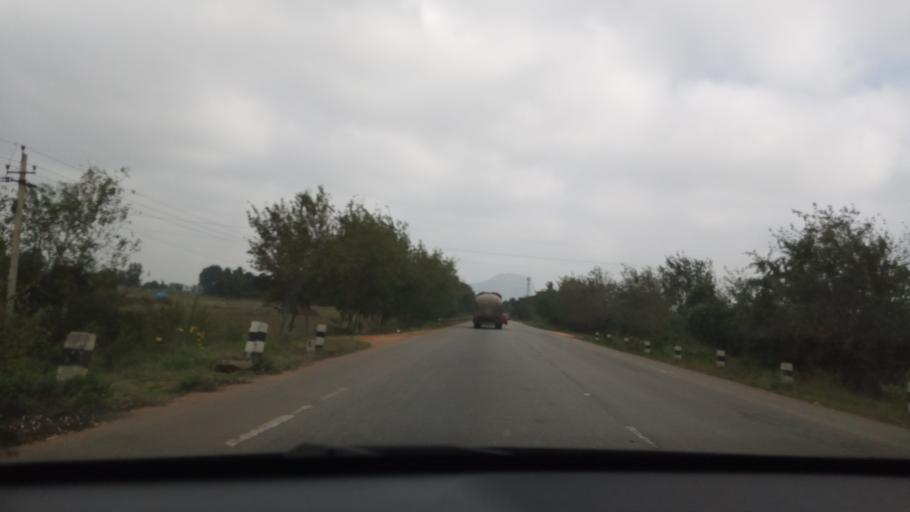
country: IN
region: Karnataka
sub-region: Chikkaballapur
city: Chintamani
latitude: 13.3103
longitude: 77.9770
